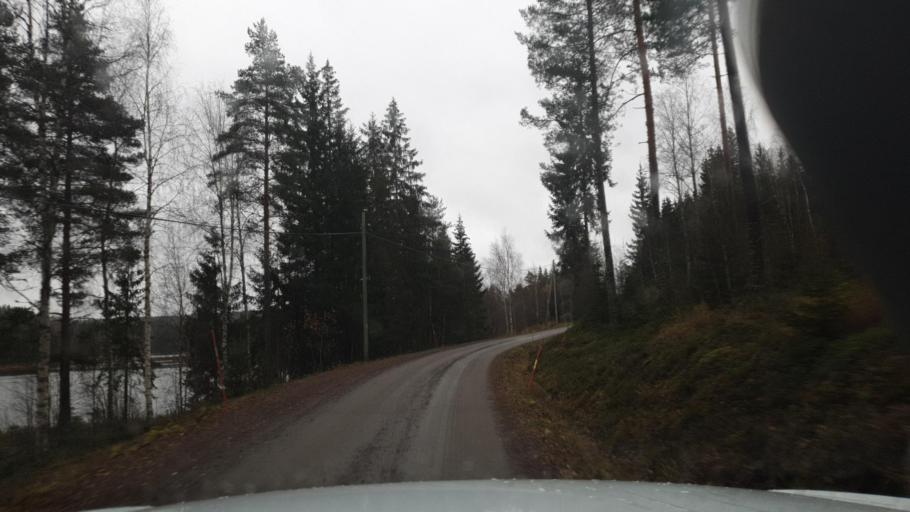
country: SE
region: Vaermland
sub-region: Eda Kommun
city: Charlottenberg
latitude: 59.9211
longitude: 12.3778
